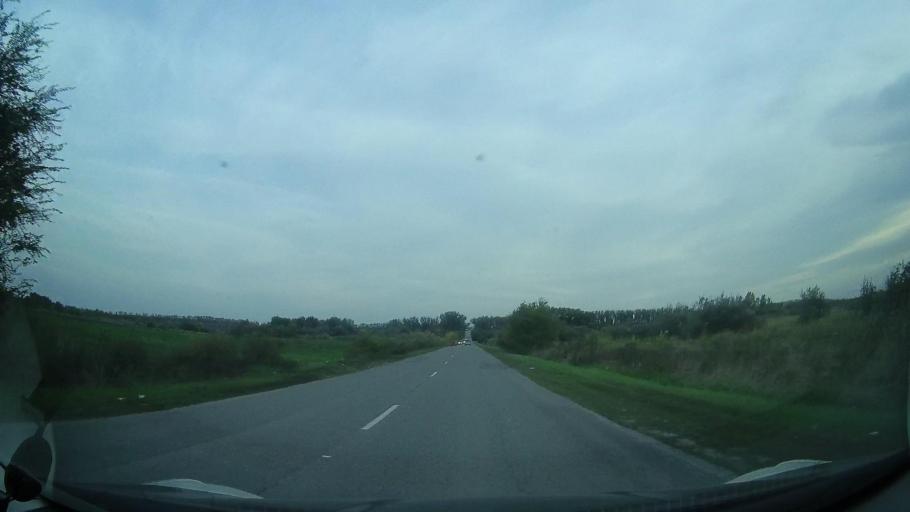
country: RU
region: Rostov
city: Ol'ginskaya
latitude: 47.1302
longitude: 39.9625
